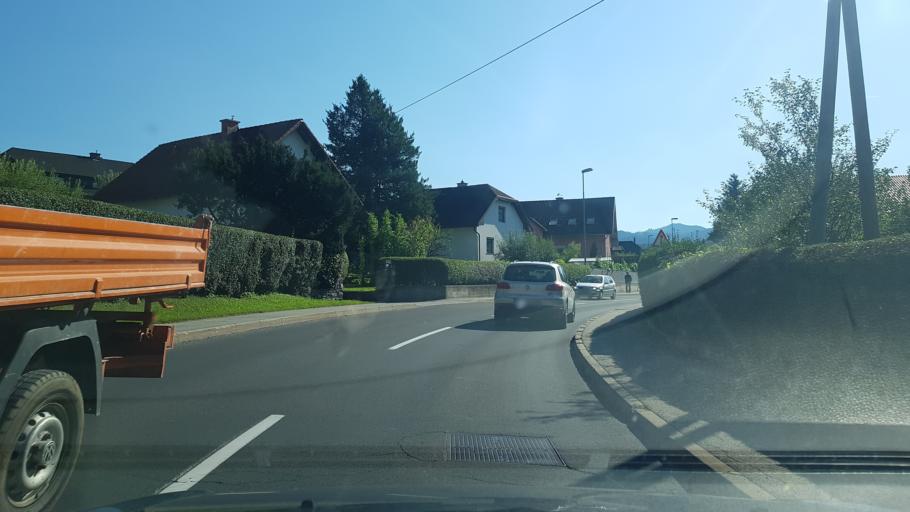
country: SI
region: Slovenj Gradec
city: Slovenj Gradec
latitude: 46.5061
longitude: 15.0761
